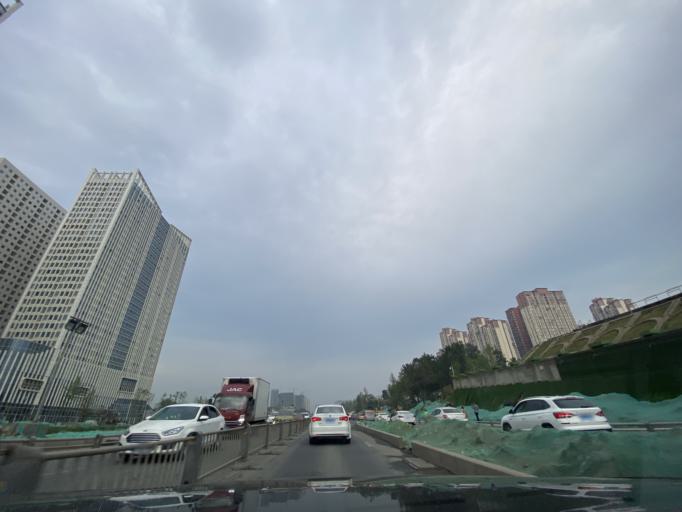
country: CN
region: Sichuan
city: Longquan
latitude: 30.6502
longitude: 104.2224
